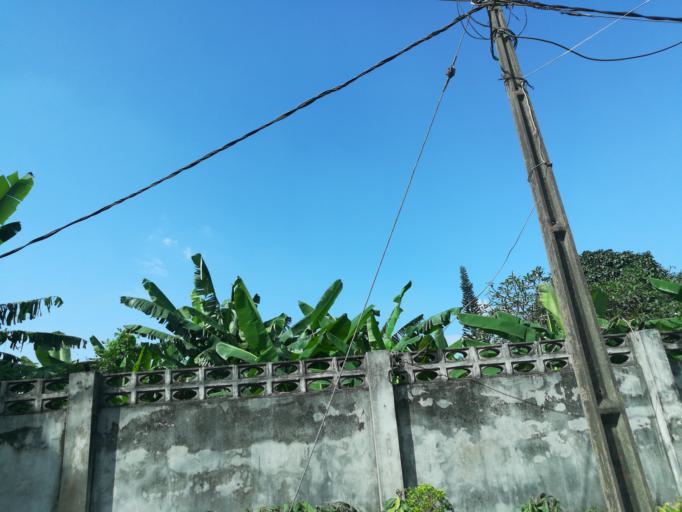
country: NG
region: Lagos
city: Ojota
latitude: 6.5751
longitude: 3.3643
